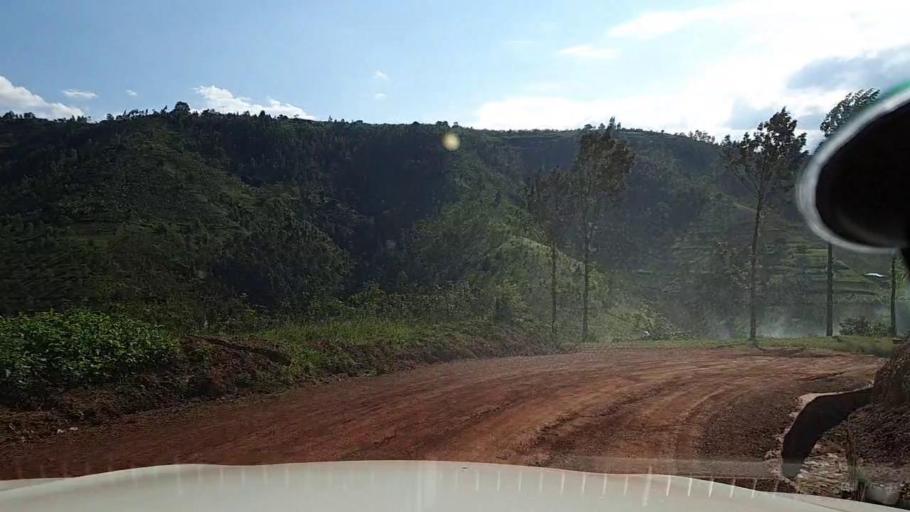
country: RW
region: Kigali
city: Kigali
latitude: -1.8453
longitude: 29.8569
